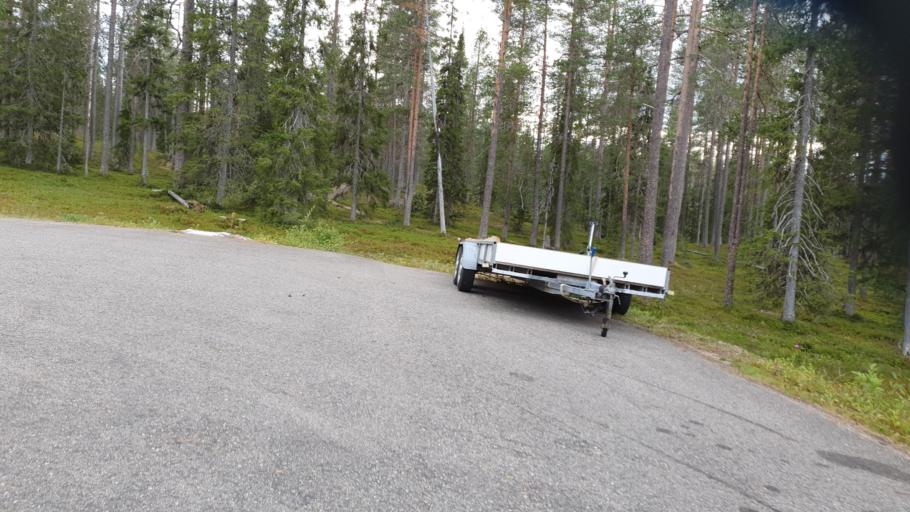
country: FI
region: Lapland
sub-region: Tunturi-Lappi
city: Kolari
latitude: 67.5928
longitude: 24.1458
